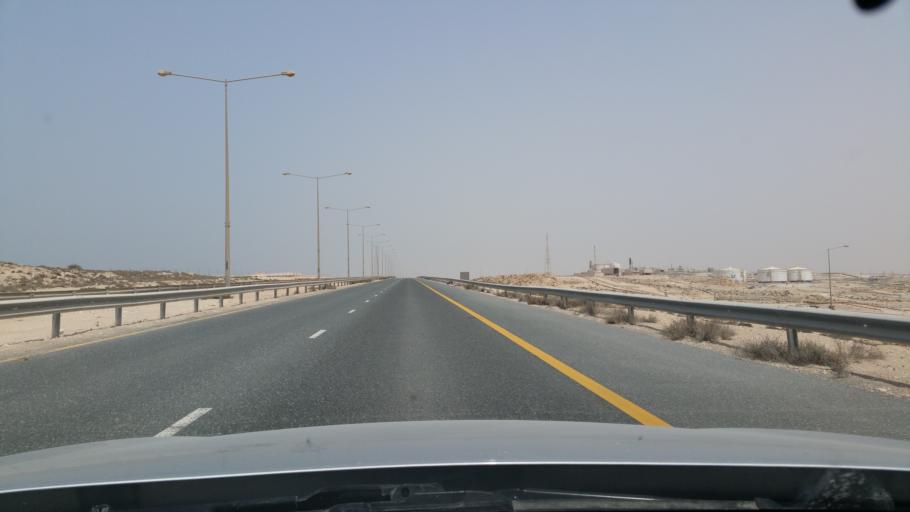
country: QA
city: Umm Bab
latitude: 25.2783
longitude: 50.7922
